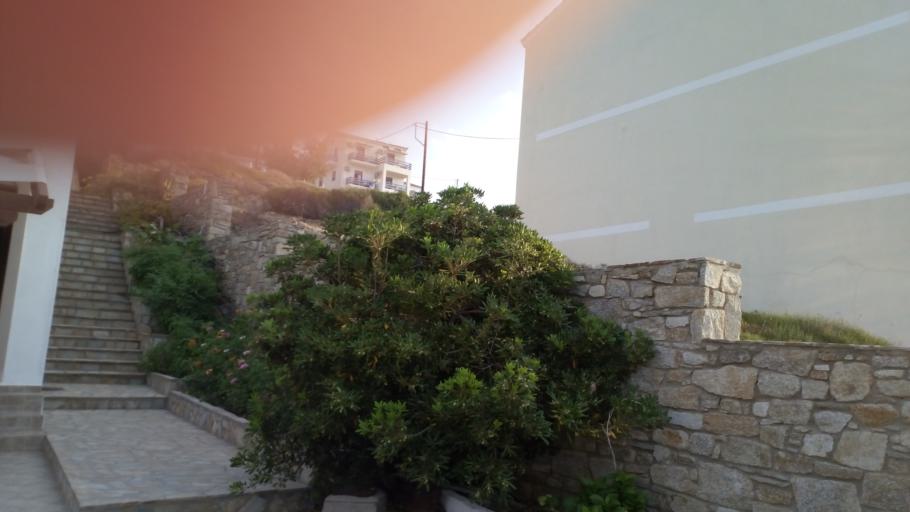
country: GR
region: North Aegean
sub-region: Nomos Samou
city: Agios Kirykos
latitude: 37.6356
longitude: 26.0849
